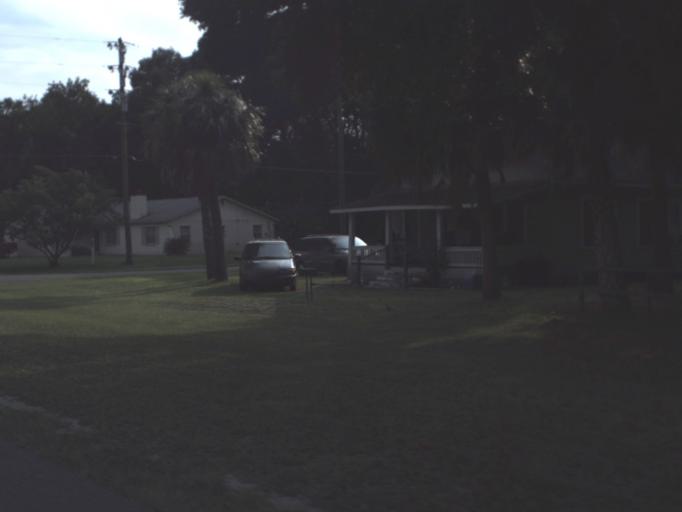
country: US
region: Florida
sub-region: Hernando County
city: Masaryktown
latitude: 28.4453
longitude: -82.4555
